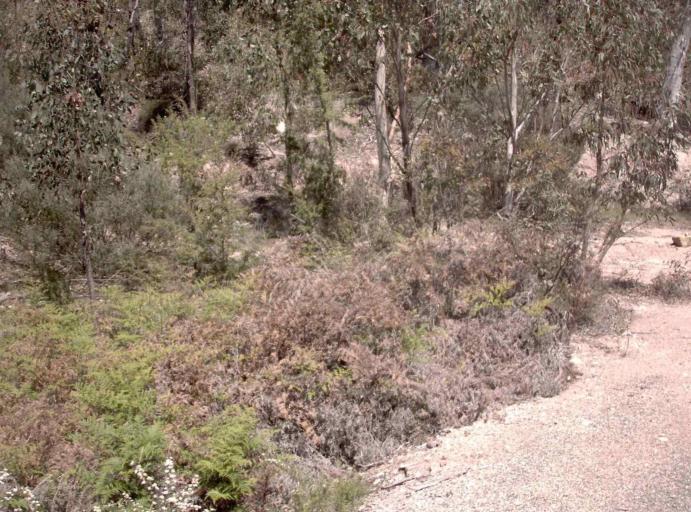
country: AU
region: New South Wales
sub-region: Snowy River
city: Jindabyne
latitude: -37.1199
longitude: 148.2436
